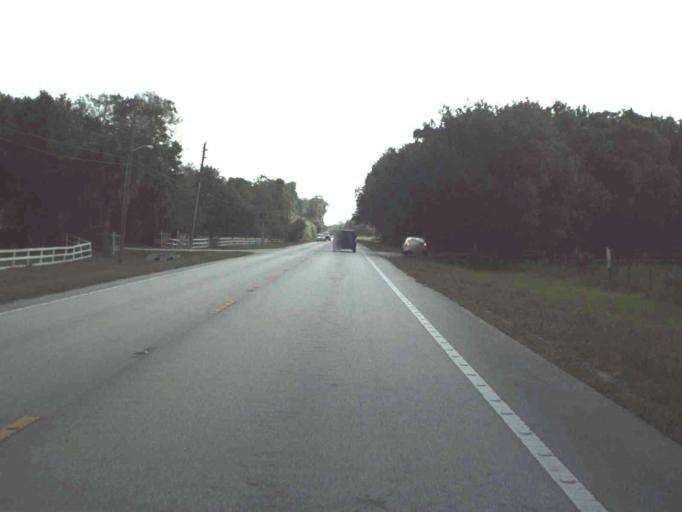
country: US
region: Florida
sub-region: Volusia County
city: Lake Helen
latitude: 28.9179
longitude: -81.1204
